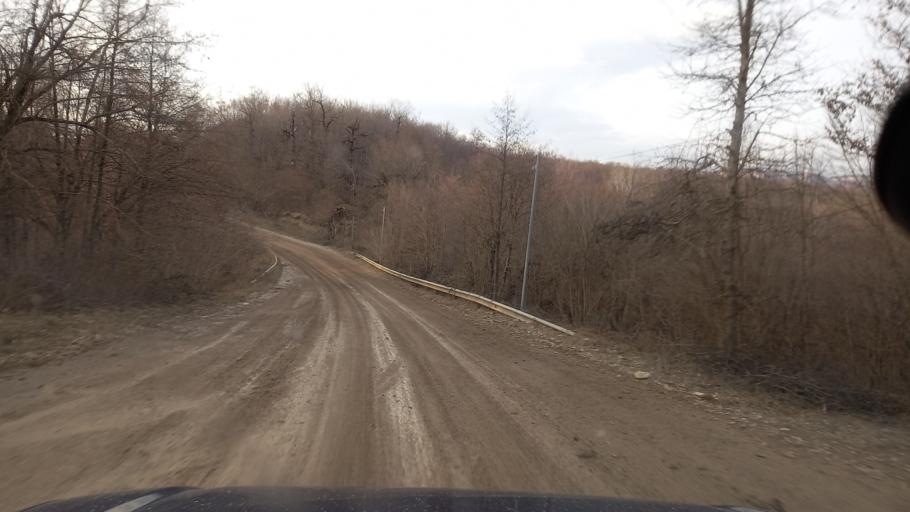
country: RU
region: Adygeya
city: Kamennomostskiy
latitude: 44.1928
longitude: 40.2591
